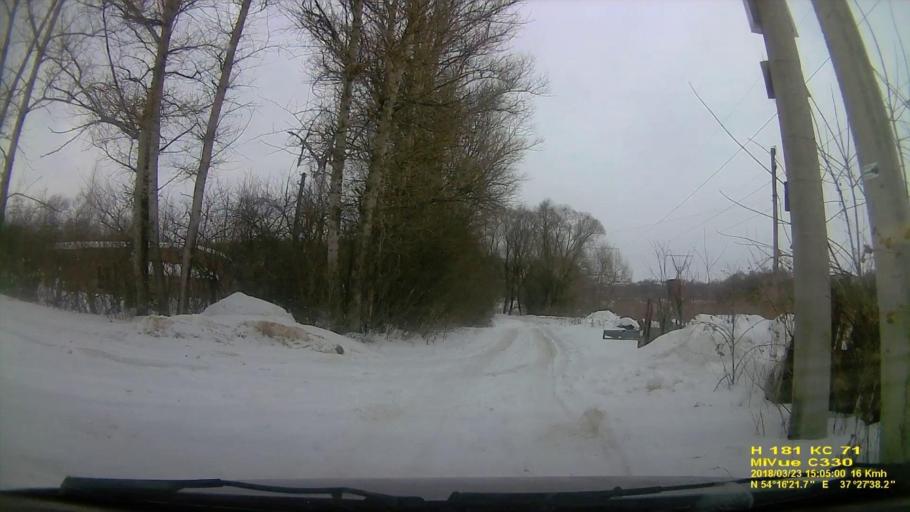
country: RU
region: Tula
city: Leninskiy
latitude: 54.2727
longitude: 37.4606
